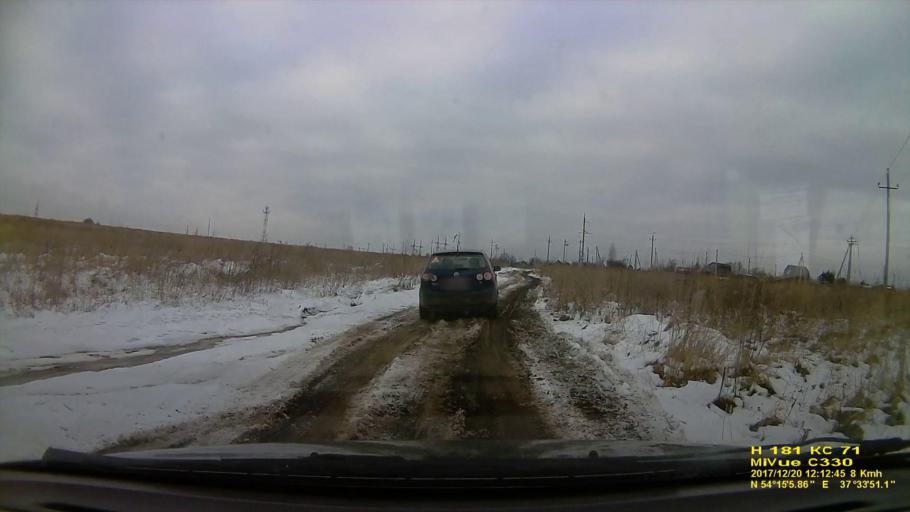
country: RU
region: Tula
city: Gorelki
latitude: 54.2516
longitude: 37.5641
